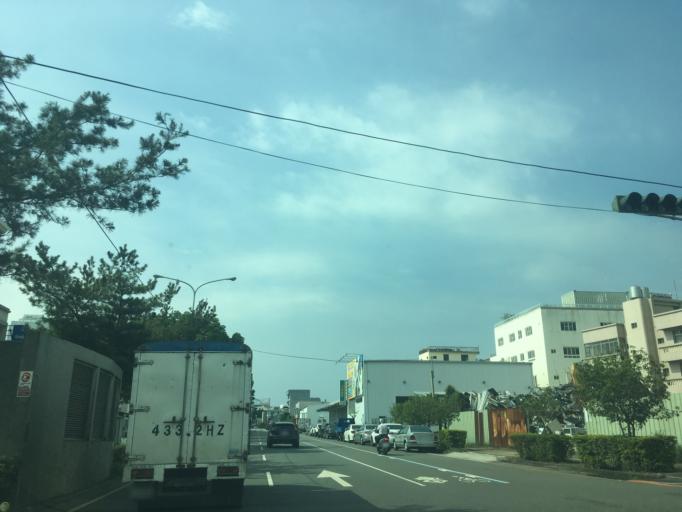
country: TW
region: Taiwan
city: Fengyuan
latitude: 24.2513
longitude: 120.7374
